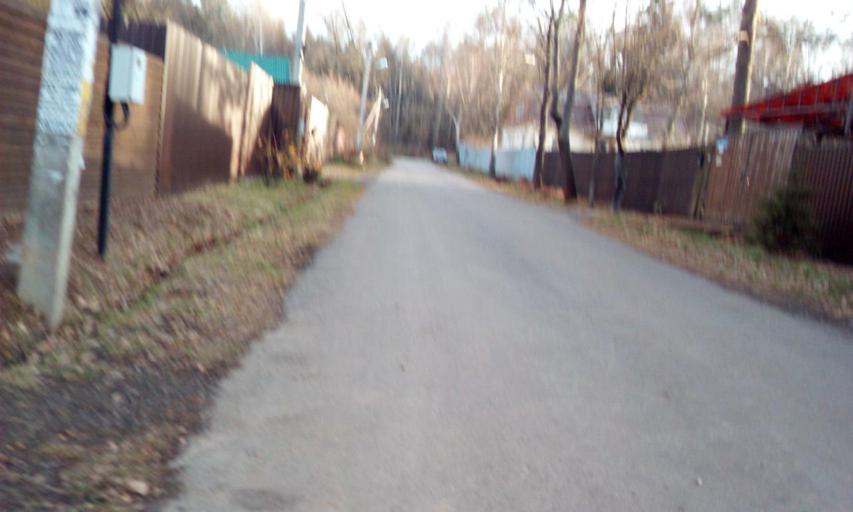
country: RU
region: Moskovskaya
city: Aprelevka
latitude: 55.5589
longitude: 37.0994
